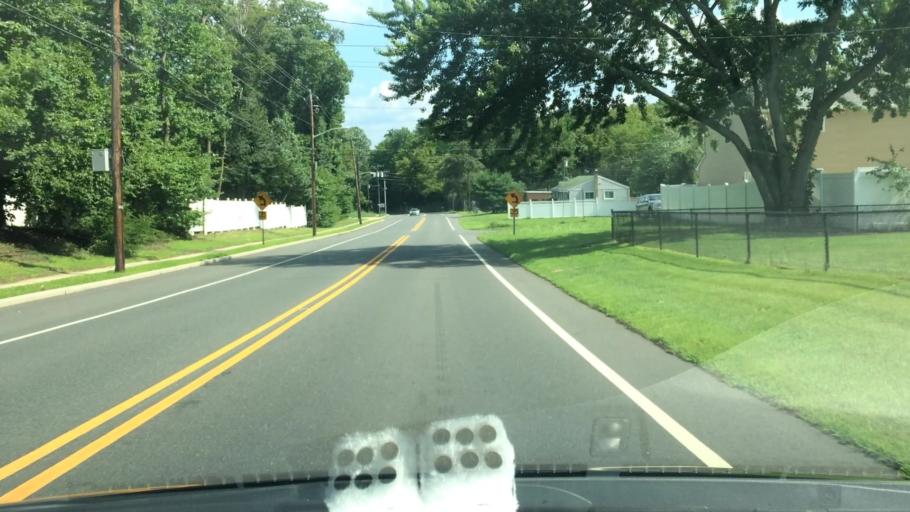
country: US
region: New Jersey
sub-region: Camden County
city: Blackwood
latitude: 39.7969
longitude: -75.0866
